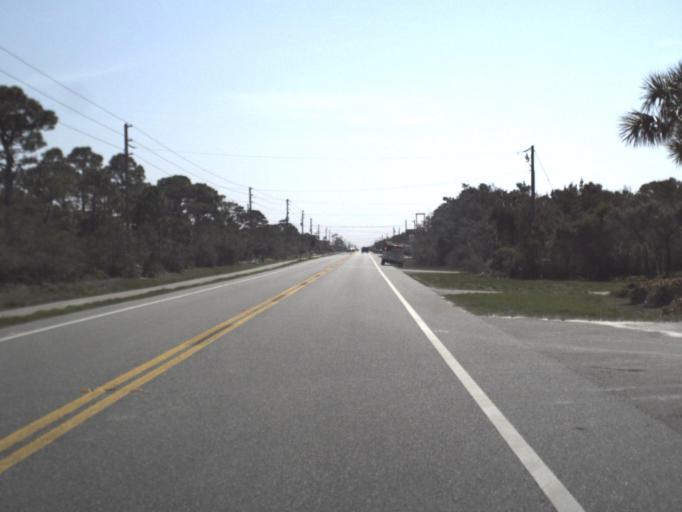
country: US
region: Florida
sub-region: Gulf County
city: Port Saint Joe
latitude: 29.7053
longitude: -85.3788
